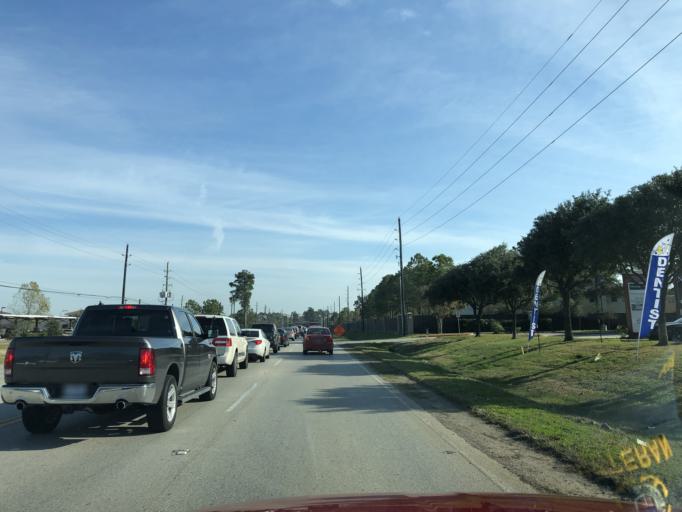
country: US
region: Texas
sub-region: Harris County
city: Tomball
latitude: 30.0360
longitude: -95.5523
